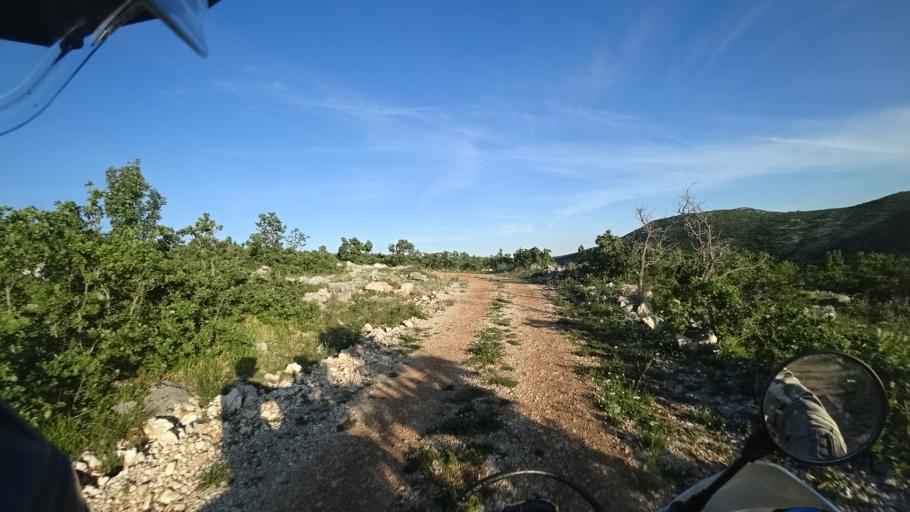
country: HR
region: Sibensko-Kniniska
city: Drnis
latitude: 43.8500
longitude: 16.3436
